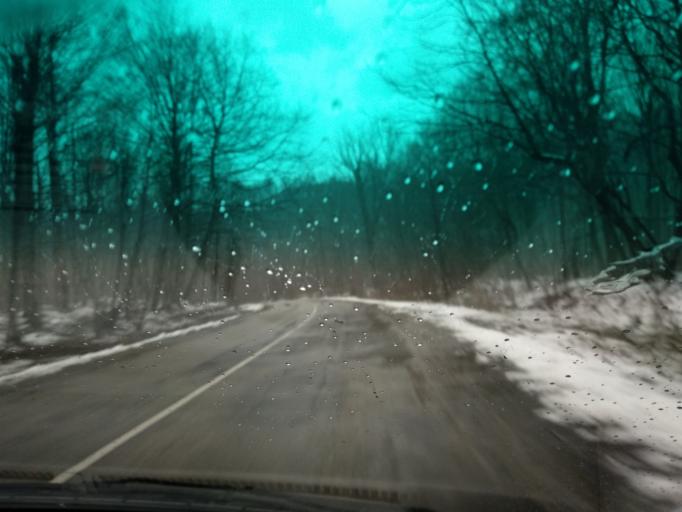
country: RU
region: Krasnodarskiy
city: Khadyzhensk
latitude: 44.2307
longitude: 39.3840
